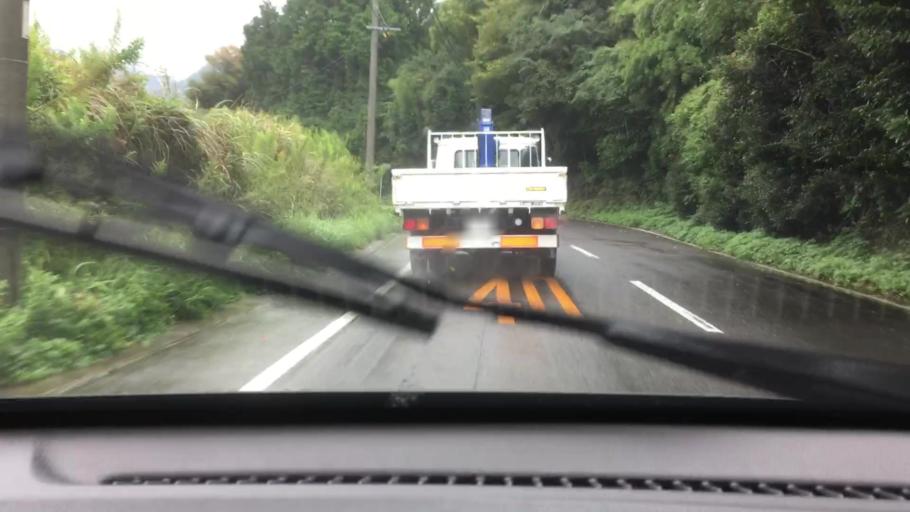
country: JP
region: Nagasaki
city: Togitsu
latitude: 32.8590
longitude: 129.7776
